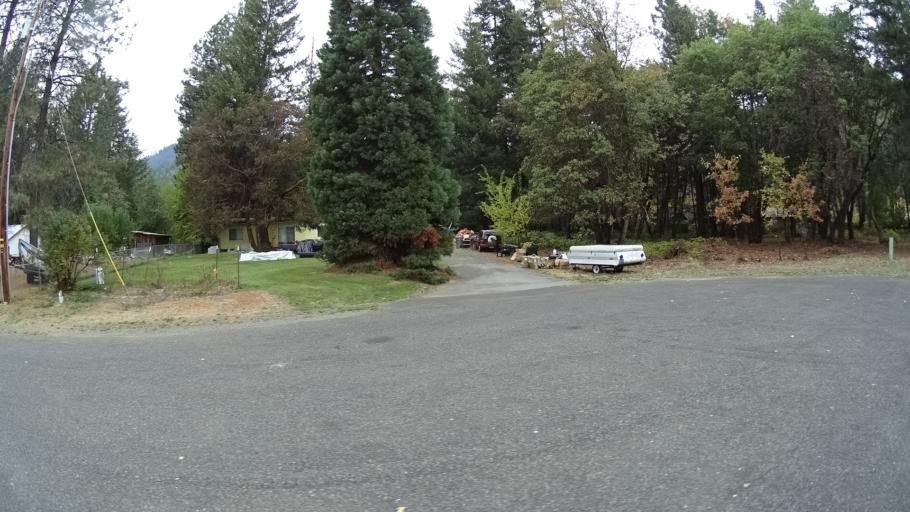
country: US
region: California
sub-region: Siskiyou County
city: Happy Camp
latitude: 41.8065
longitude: -123.3819
